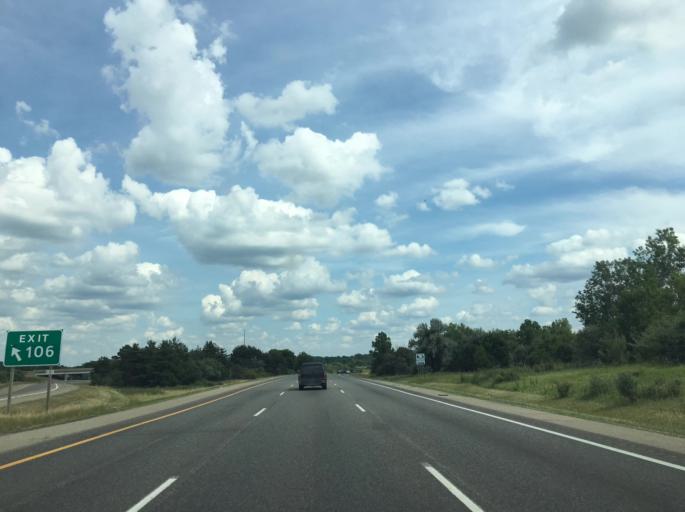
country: US
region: Michigan
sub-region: Genesee County
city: Grand Blanc
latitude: 42.8747
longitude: -83.6010
